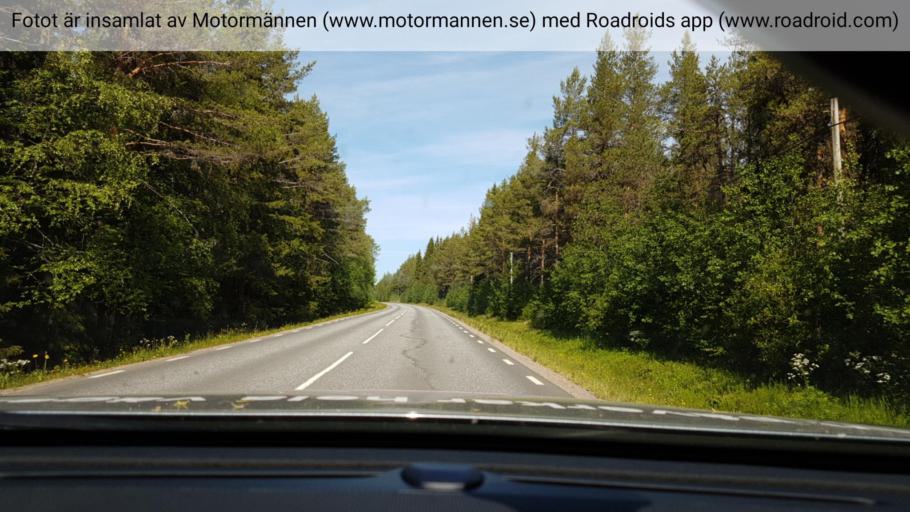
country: SE
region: Vaesterbotten
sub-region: Dorotea Kommun
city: Dorotea
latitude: 64.2621
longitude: 16.3682
